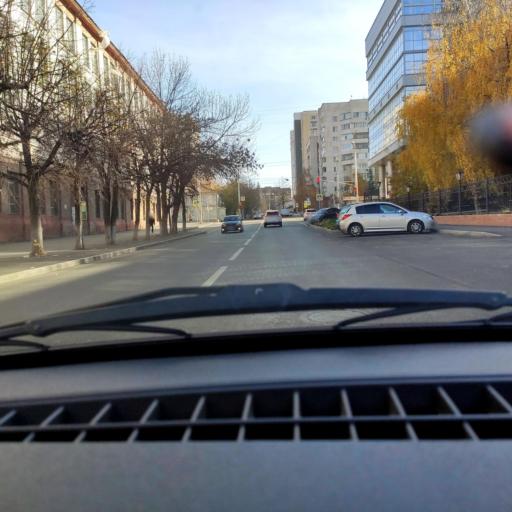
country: RU
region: Bashkortostan
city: Ufa
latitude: 54.7332
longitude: 55.9365
